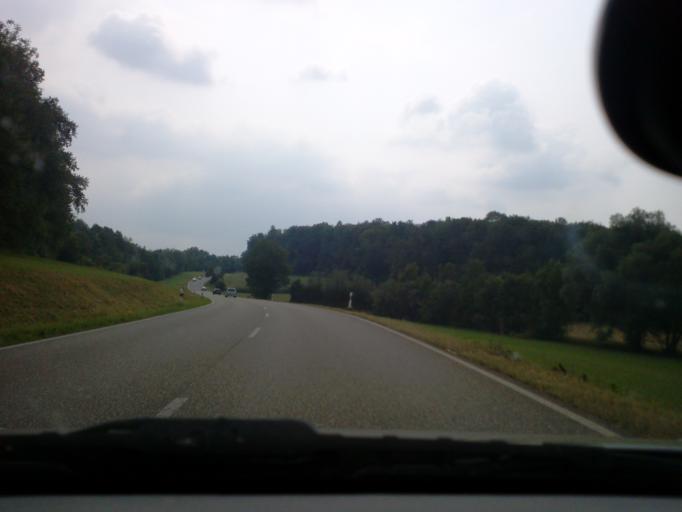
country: DE
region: Baden-Wuerttemberg
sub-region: Karlsruhe Region
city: Gondelsheim
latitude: 49.0300
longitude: 8.6586
